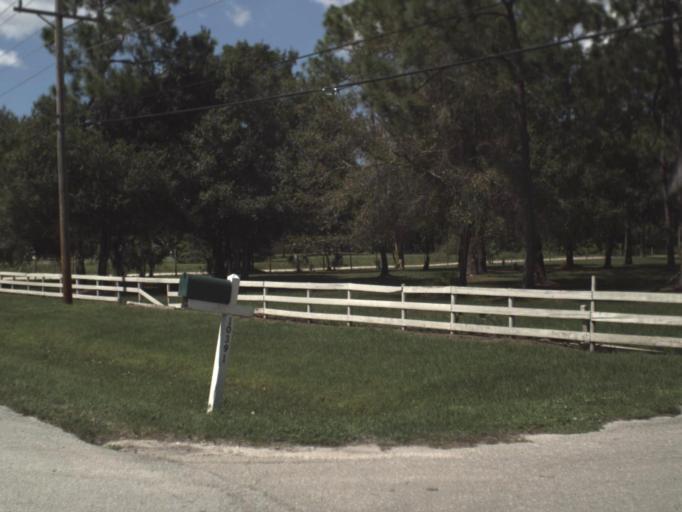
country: US
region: Florida
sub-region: Lee County
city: Fort Myers Shores
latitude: 26.7150
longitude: -81.7872
